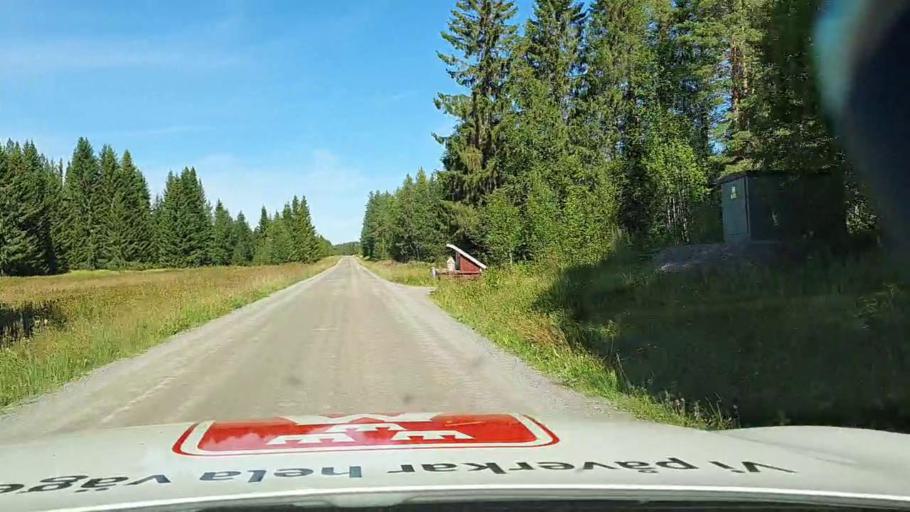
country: SE
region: Jaemtland
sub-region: Stroemsunds Kommun
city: Stroemsund
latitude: 63.6830
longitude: 15.3882
